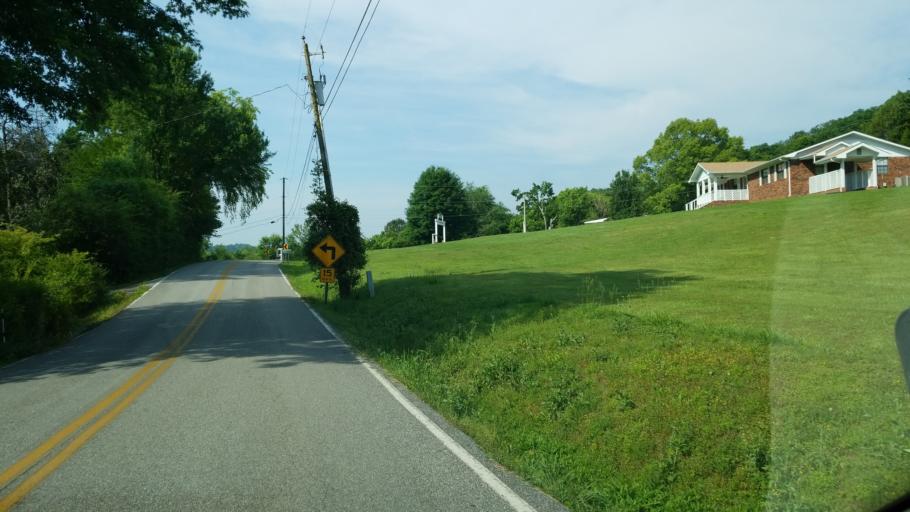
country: US
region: Tennessee
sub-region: Hamilton County
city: Collegedale
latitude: 35.0846
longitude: -85.0288
